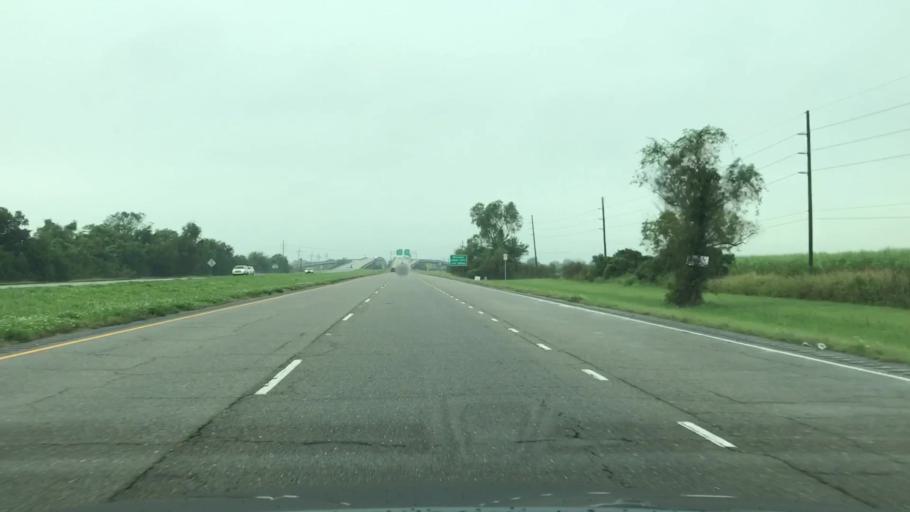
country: US
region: Louisiana
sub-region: Lafourche Parish
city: Mathews
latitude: 29.7162
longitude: -90.5647
